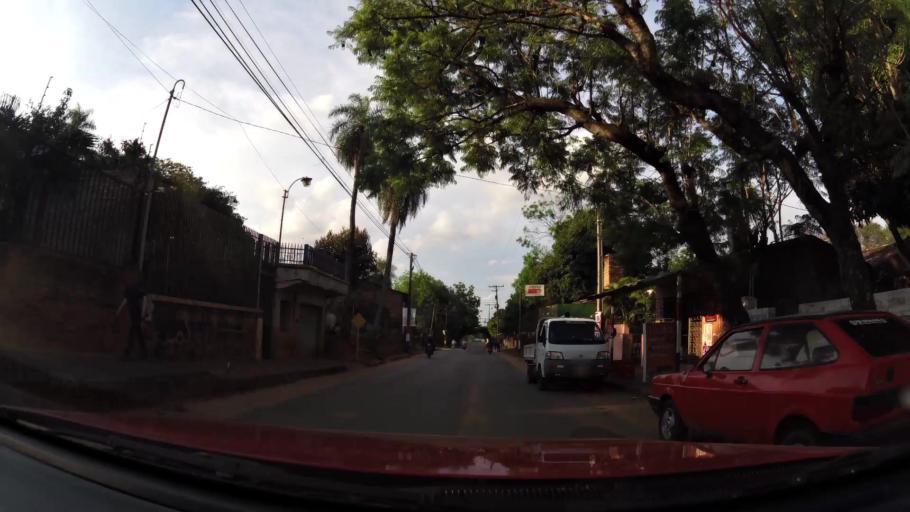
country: PY
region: Central
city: Fernando de la Mora
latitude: -25.3556
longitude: -57.5284
